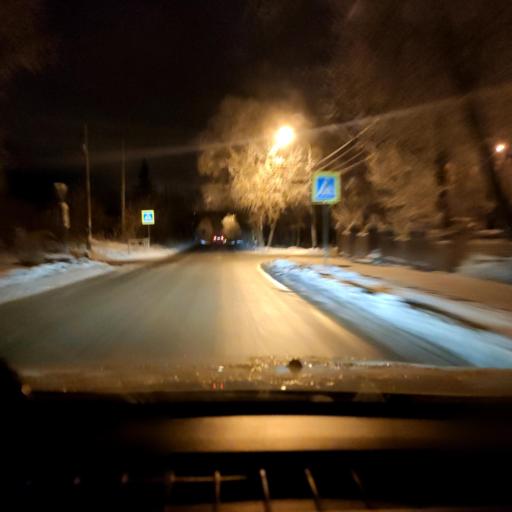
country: RU
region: Samara
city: Novosemeykino
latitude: 53.3437
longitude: 50.2283
